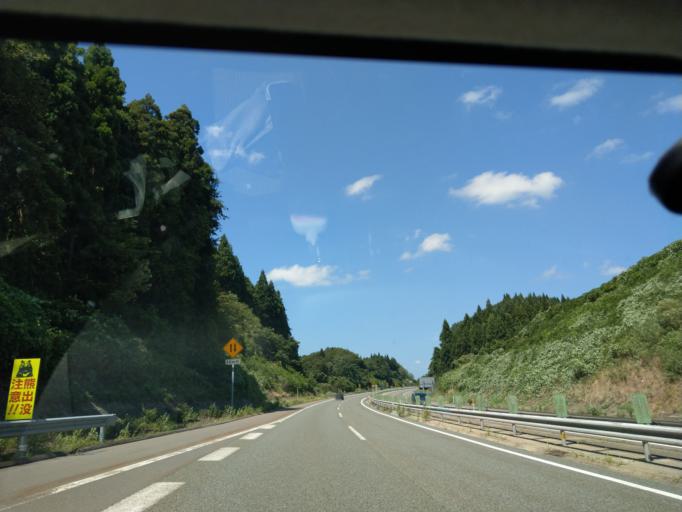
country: JP
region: Akita
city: Akita
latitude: 39.6624
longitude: 140.1894
